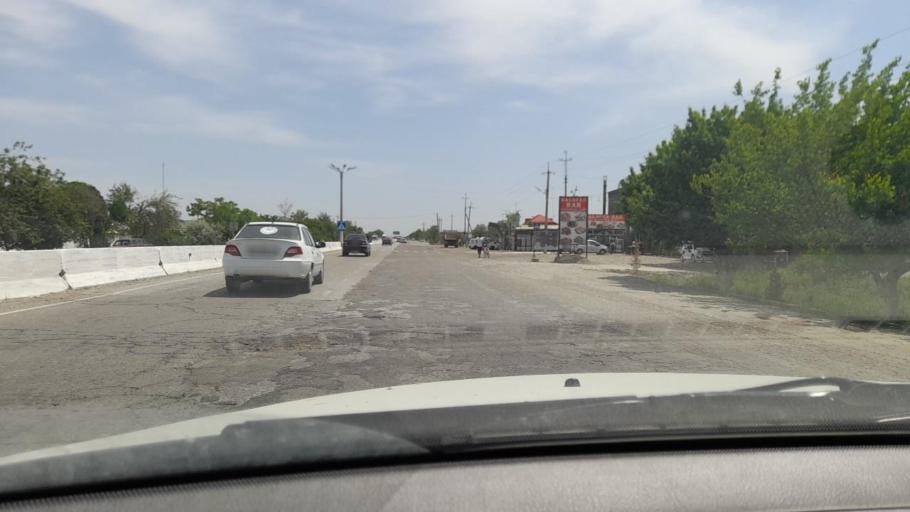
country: UZ
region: Bukhara
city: Ghijduwon
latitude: 40.0903
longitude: 64.6564
